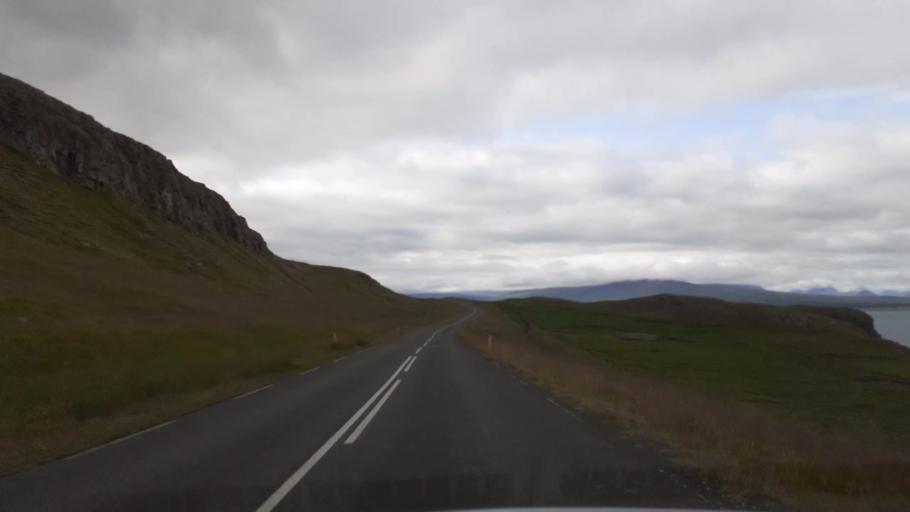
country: IS
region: Northeast
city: Akureyri
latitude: 65.8109
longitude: -18.0530
